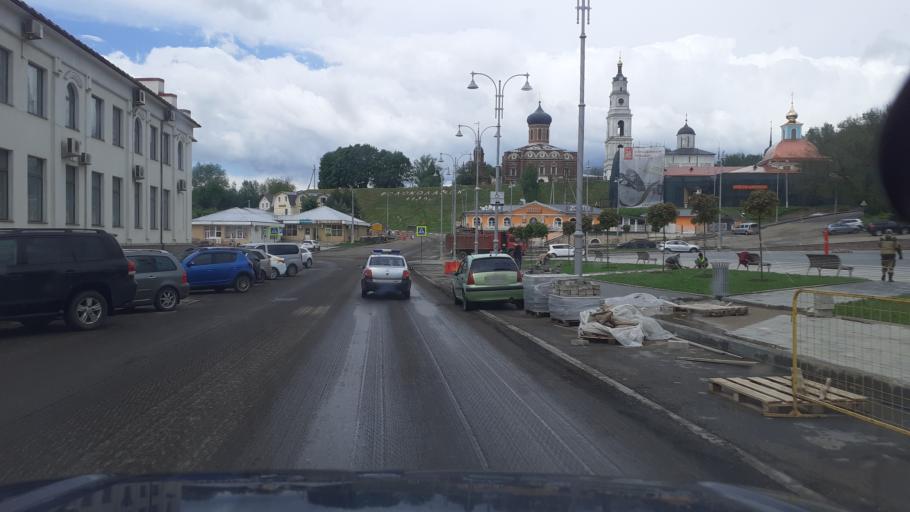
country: RU
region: Moskovskaya
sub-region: Volokolamskiy Rayon
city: Volokolamsk
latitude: 56.0356
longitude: 35.9580
